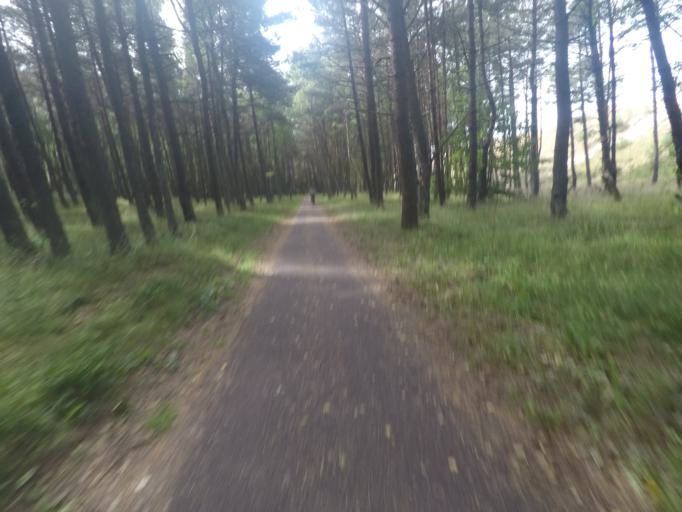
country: LT
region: Klaipedos apskritis
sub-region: Klaipeda
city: Klaipeda
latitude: 55.6664
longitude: 21.1060
